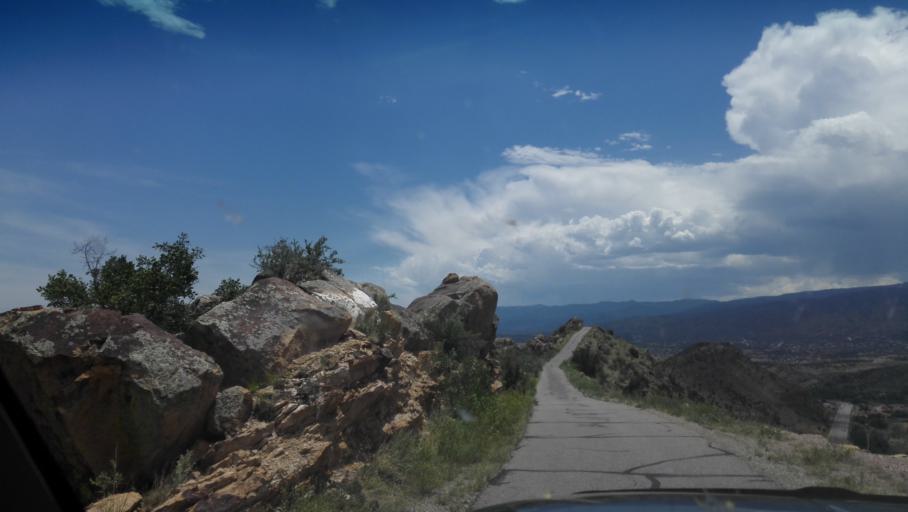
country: US
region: Colorado
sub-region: Fremont County
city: Canon City
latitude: 38.4557
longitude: -105.2499
